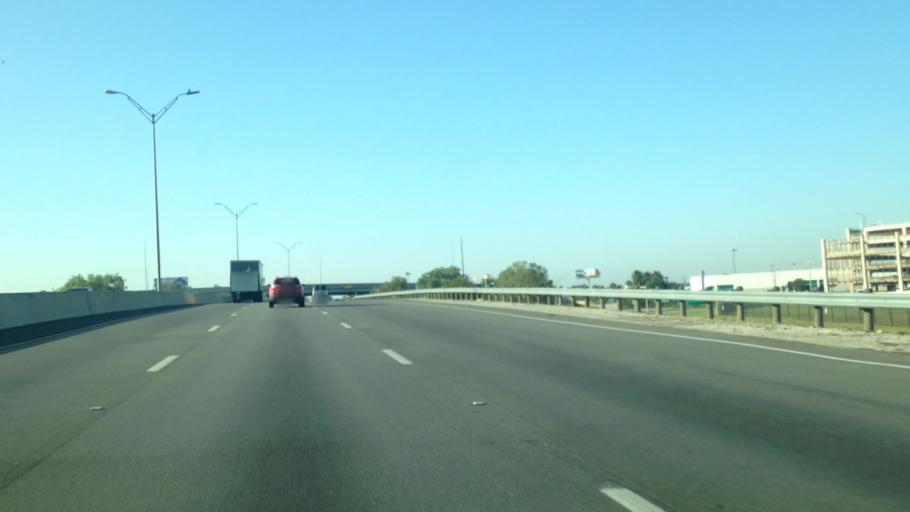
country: US
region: Texas
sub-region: Bexar County
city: Kirby
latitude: 29.4580
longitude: -98.4124
